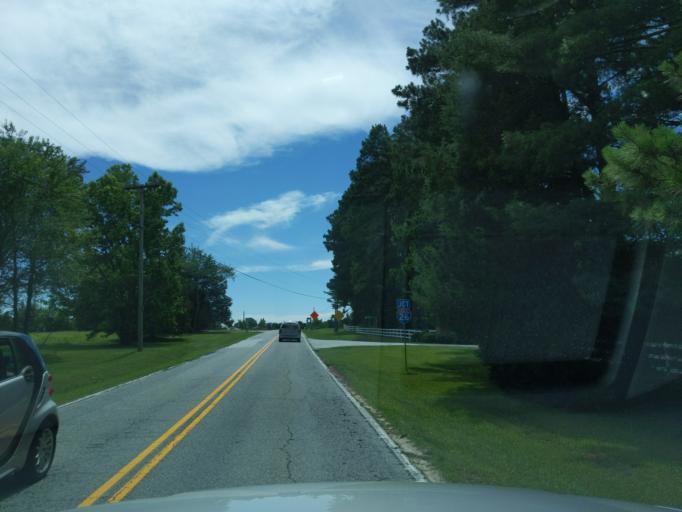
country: US
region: South Carolina
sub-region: Spartanburg County
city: Landrum
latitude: 35.1846
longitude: -82.1540
